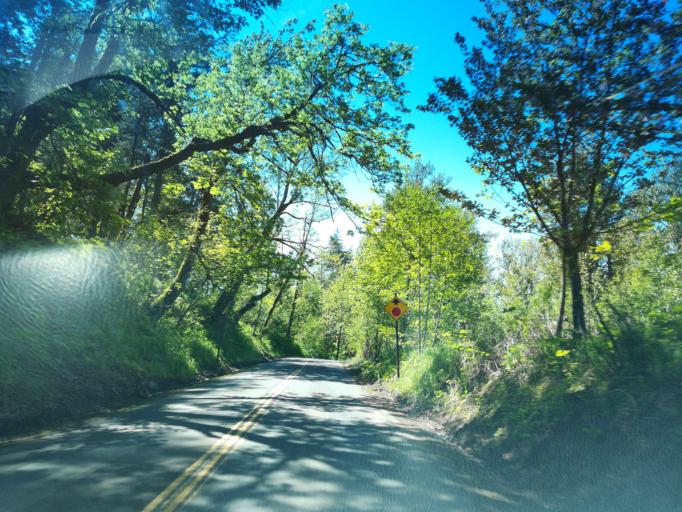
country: US
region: Oregon
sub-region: Multnomah County
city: Troutdale
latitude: 45.5099
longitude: -122.3642
